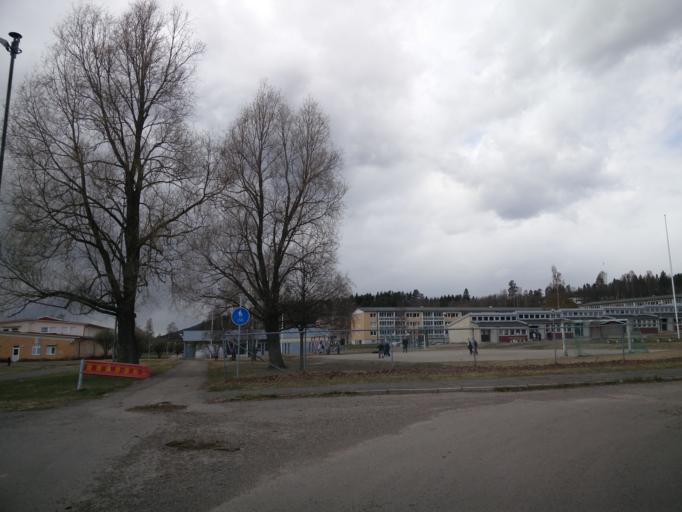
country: SE
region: Vaesternorrland
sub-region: Sundsvalls Kommun
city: Sundsvall
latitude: 62.4033
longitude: 17.2578
